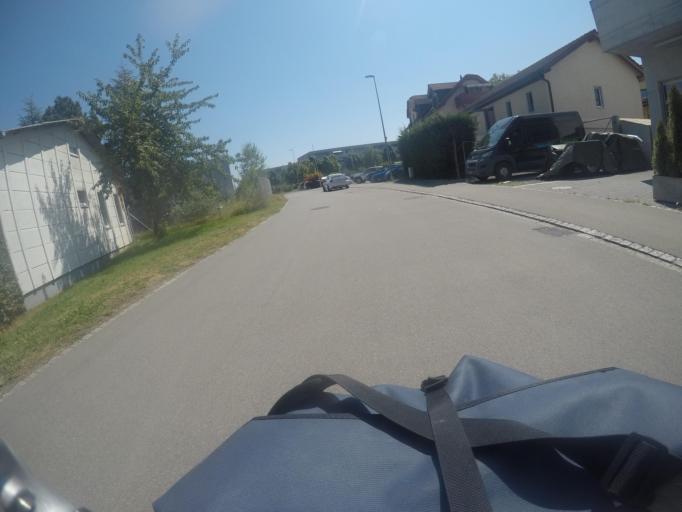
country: CH
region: Thurgau
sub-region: Arbon District
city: Arbon
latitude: 47.5042
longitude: 9.4314
